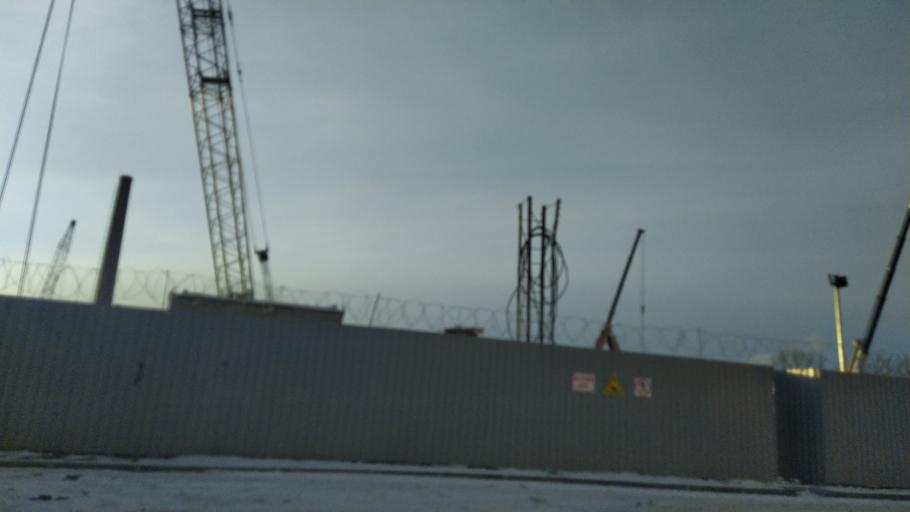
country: RU
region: St.-Petersburg
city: Admiralteisky
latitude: 59.9044
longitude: 30.3089
